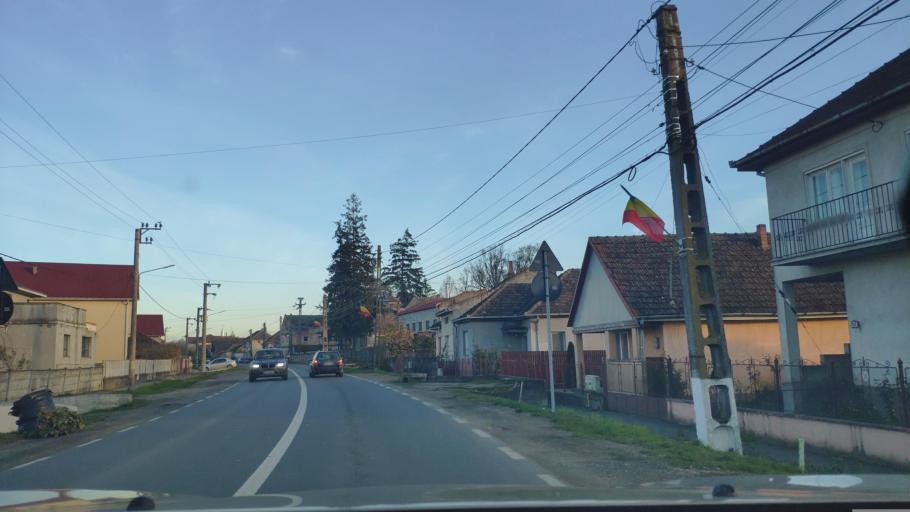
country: RO
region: Satu Mare
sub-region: Comuna Odoreu
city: Odoreu
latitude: 47.7958
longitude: 22.9857
